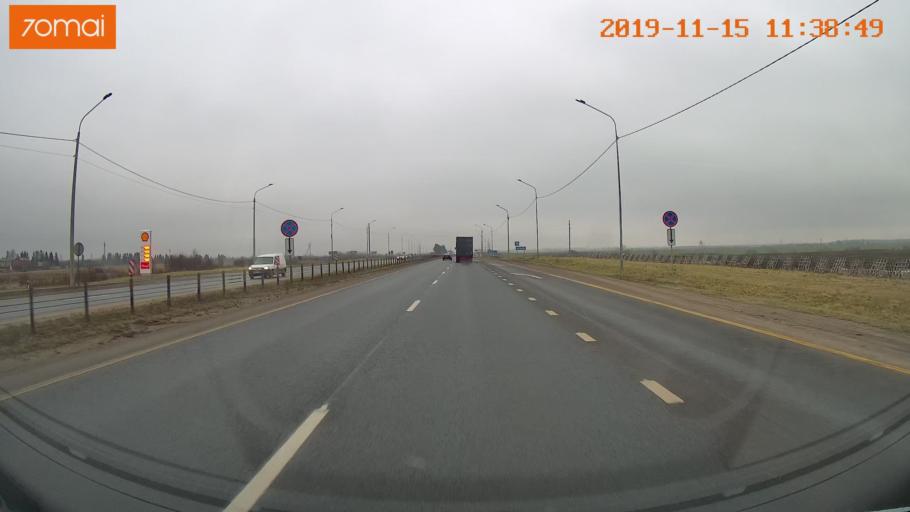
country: RU
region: Vologda
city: Molochnoye
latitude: 59.2107
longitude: 39.7078
